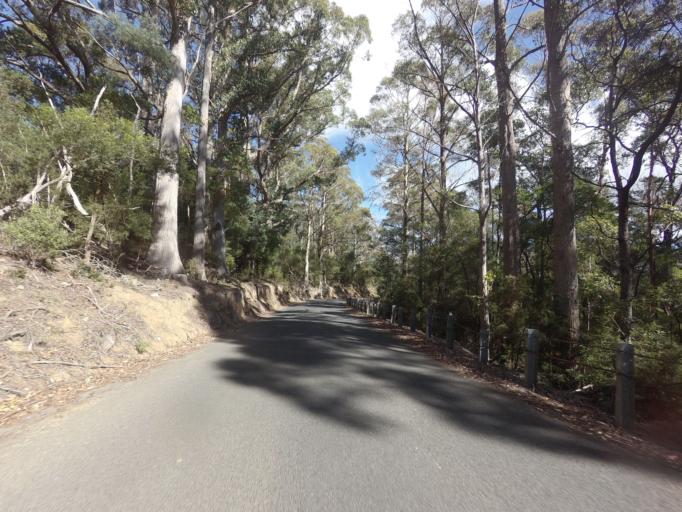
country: AU
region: Tasmania
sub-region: Break O'Day
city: St Helens
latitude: -41.6377
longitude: 148.2429
